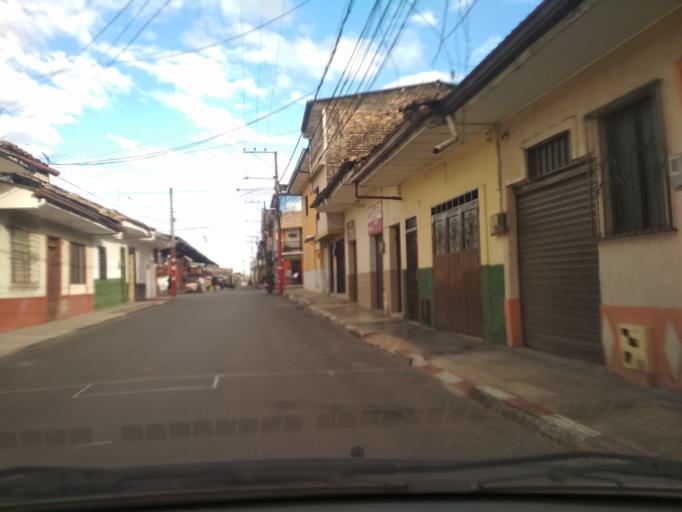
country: CO
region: Cauca
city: Popayan
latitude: 2.4353
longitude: -76.6078
